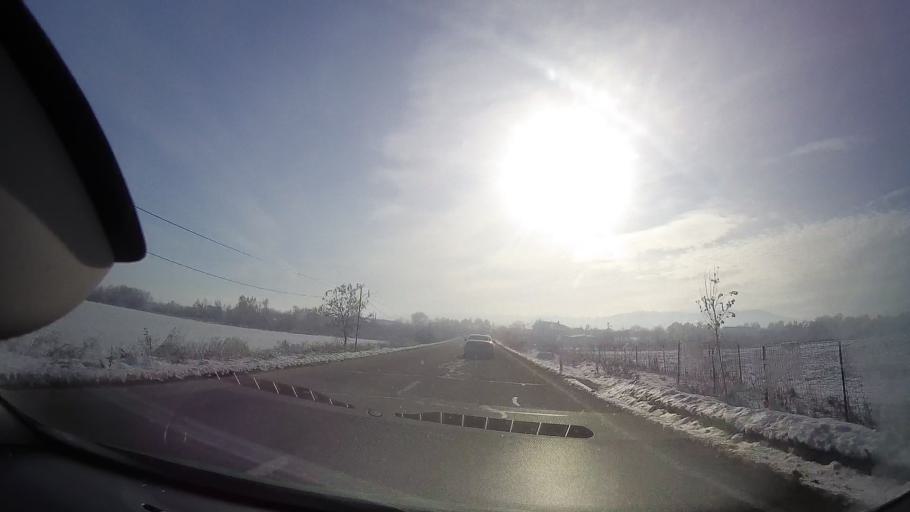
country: RO
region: Neamt
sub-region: Comuna Dobreni
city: Dobreni
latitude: 47.0049
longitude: 26.4240
